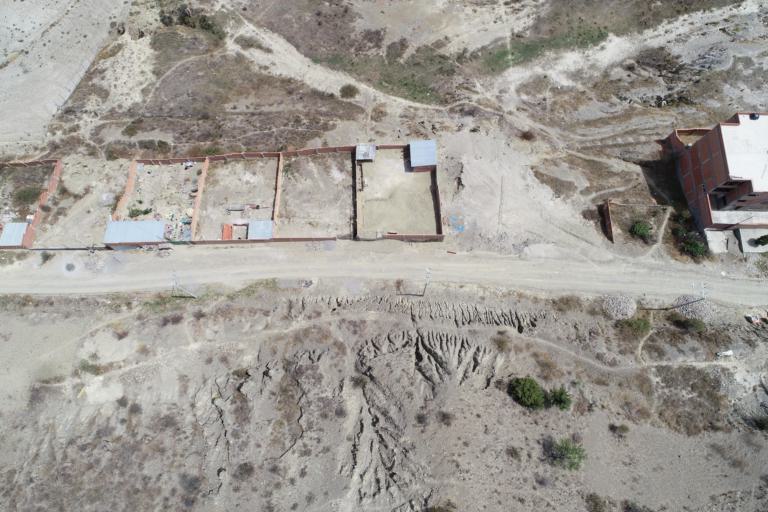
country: BO
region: La Paz
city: La Paz
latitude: -16.5183
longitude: -68.0771
